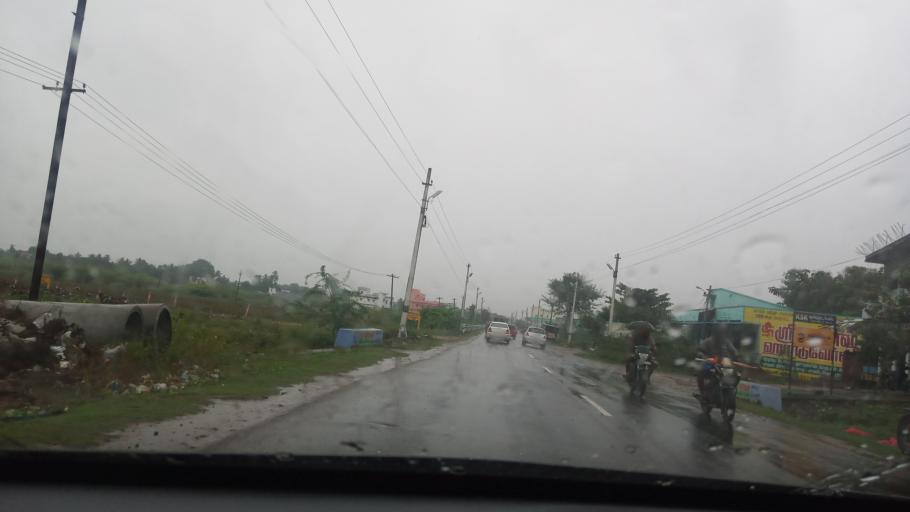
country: IN
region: Tamil Nadu
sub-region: Tiruvannamalai
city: Cheyyar
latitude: 12.6582
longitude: 79.5373
